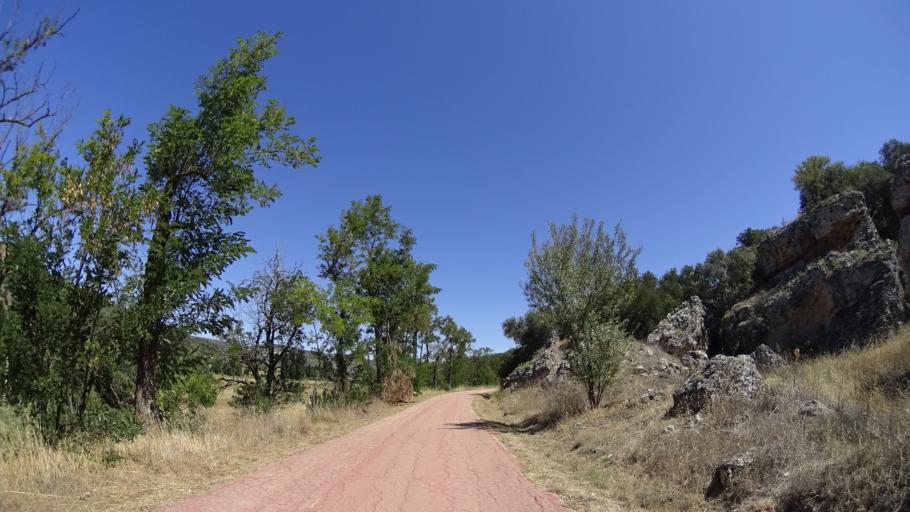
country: ES
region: Madrid
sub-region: Provincia de Madrid
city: Ambite
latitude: 40.2984
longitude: -3.1943
